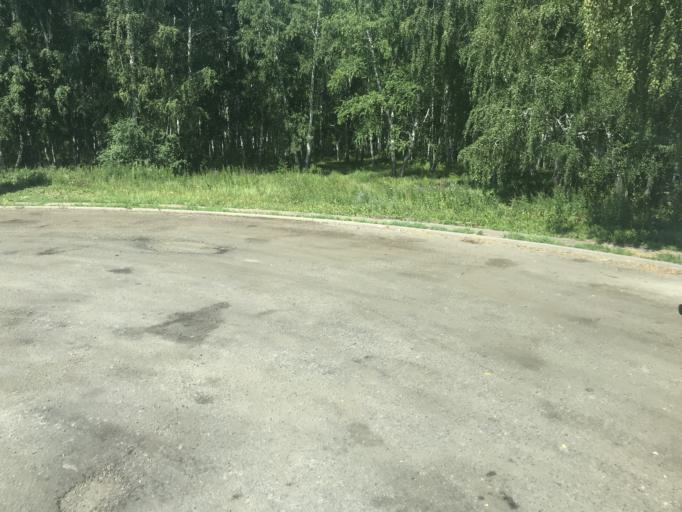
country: KZ
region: Soltustik Qazaqstan
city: Bishkul
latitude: 54.6639
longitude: 69.1468
